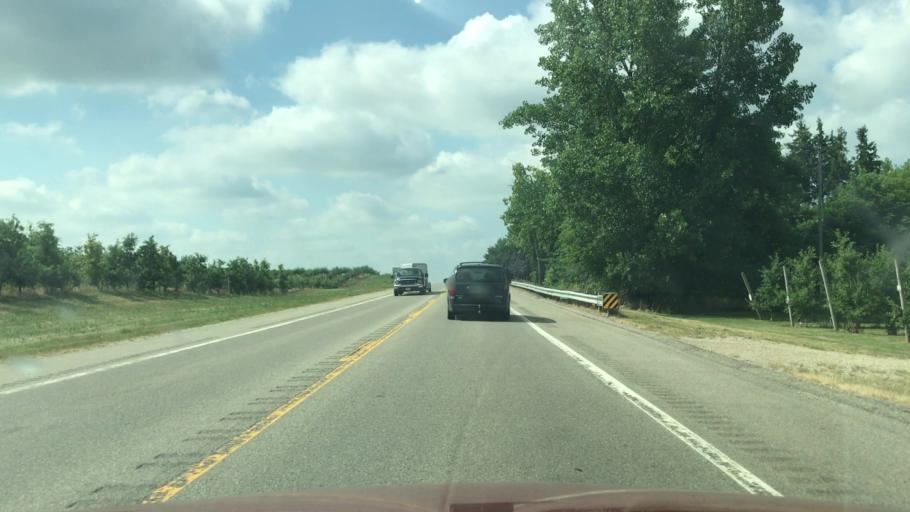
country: US
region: Michigan
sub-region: Kent County
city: Kent City
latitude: 43.2427
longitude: -85.8106
